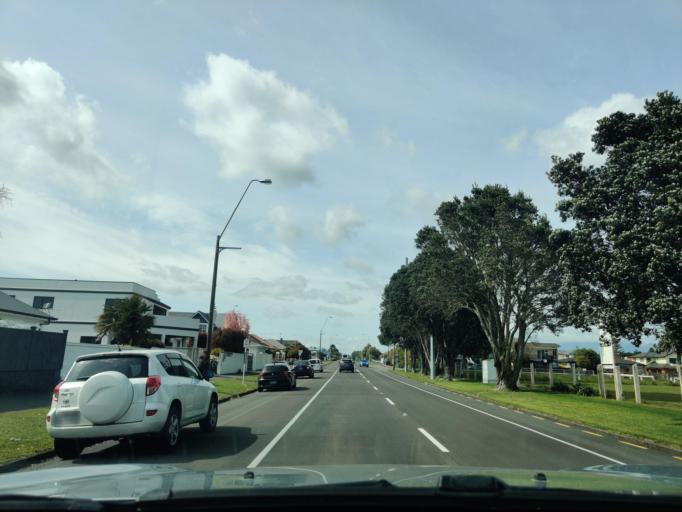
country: NZ
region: Taranaki
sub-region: New Plymouth District
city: New Plymouth
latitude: -39.0677
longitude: 174.0890
